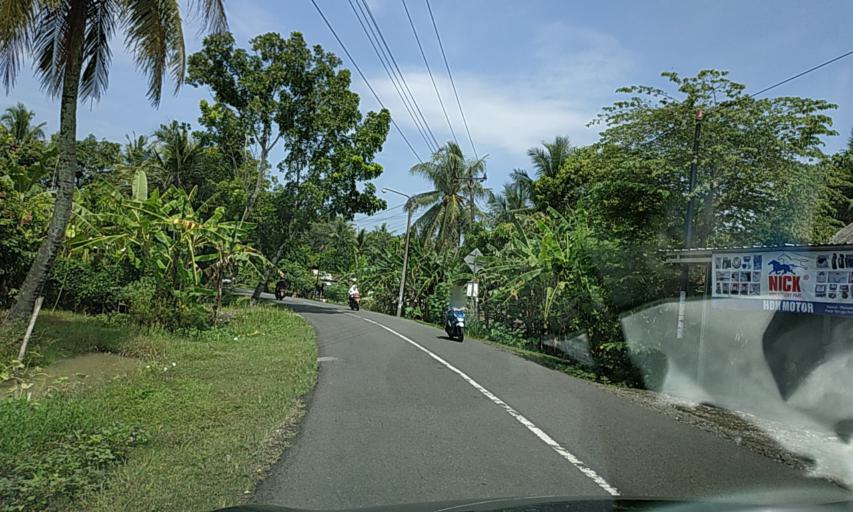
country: ID
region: Central Java
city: Kedungbulu
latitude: -7.5265
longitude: 108.7834
